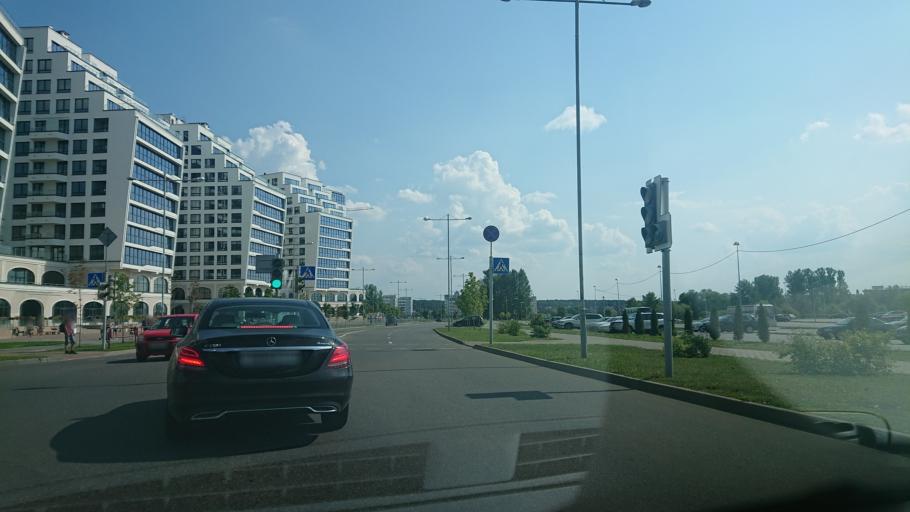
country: BY
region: Minsk
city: Borovlyany
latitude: 53.9323
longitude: 27.6492
